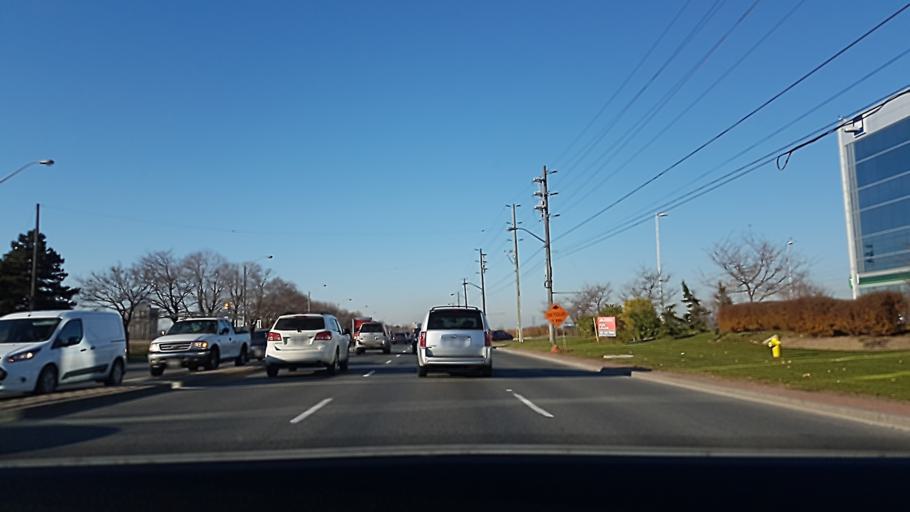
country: CA
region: Ontario
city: Concord
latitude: 43.7816
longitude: -79.4948
